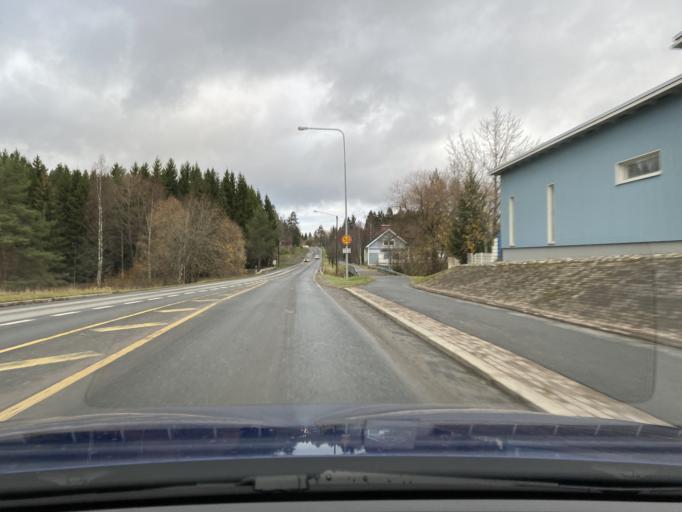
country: FI
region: Pirkanmaa
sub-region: Tampere
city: Lempaeaelae
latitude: 61.3840
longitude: 23.7806
